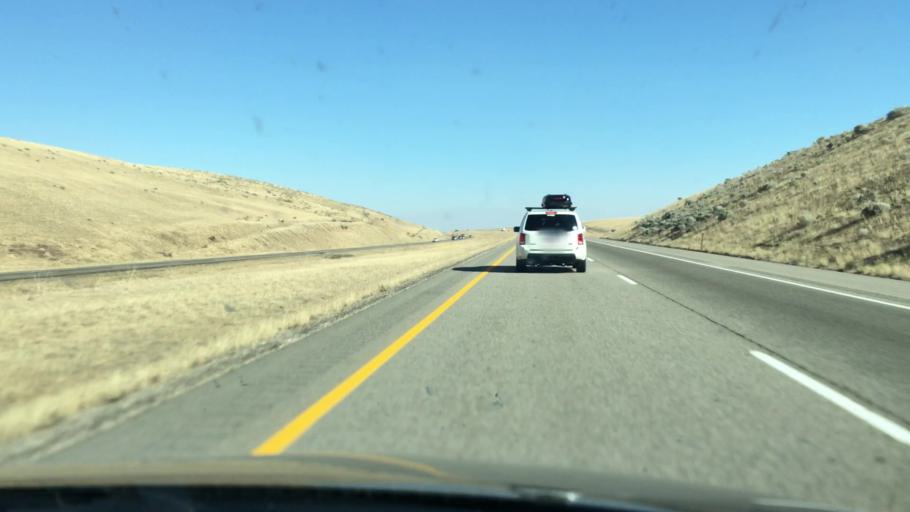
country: US
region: Idaho
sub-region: Ada County
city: Boise
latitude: 43.4957
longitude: -116.1315
